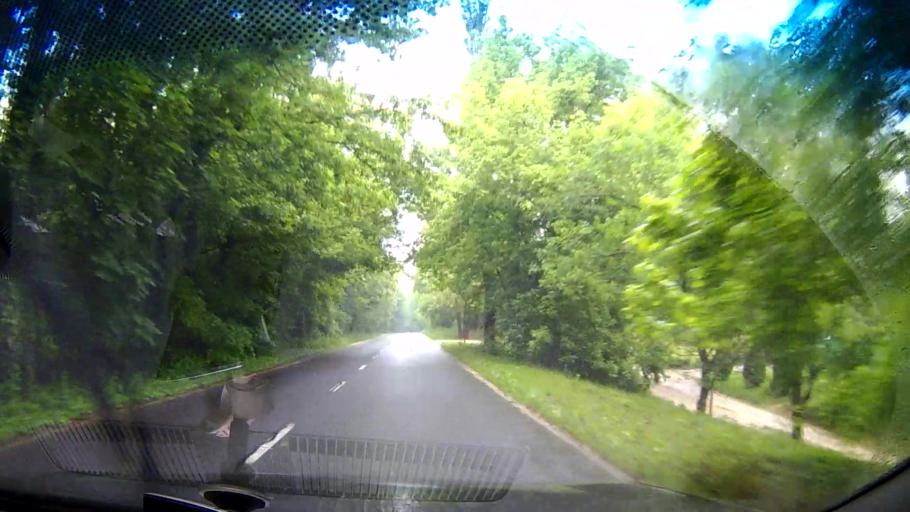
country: HU
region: Komarom-Esztergom
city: Tata
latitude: 47.6240
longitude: 18.3372
